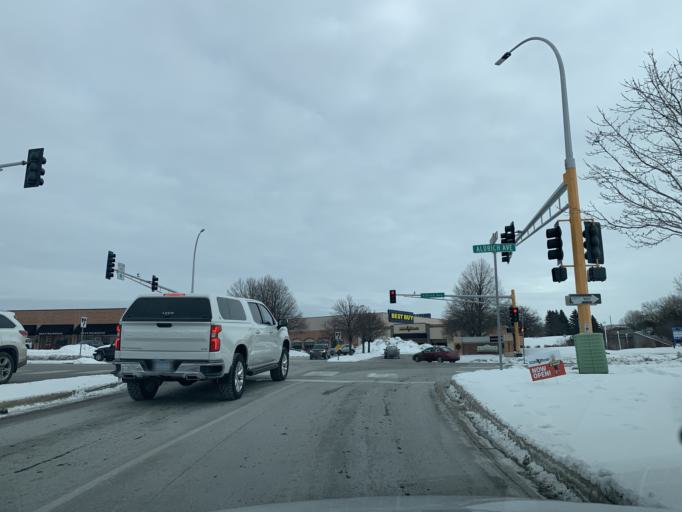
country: US
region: Minnesota
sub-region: Dakota County
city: Burnsville
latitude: 44.7478
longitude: -93.2884
